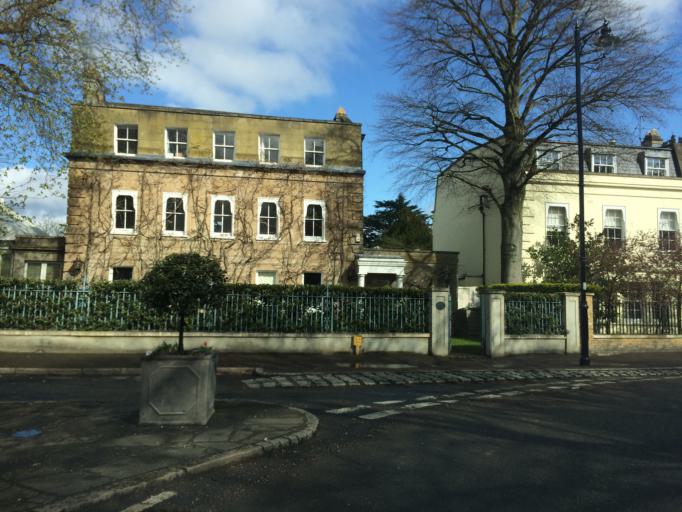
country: GB
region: England
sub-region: Surrey
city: Staines
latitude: 51.4092
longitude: -0.4902
